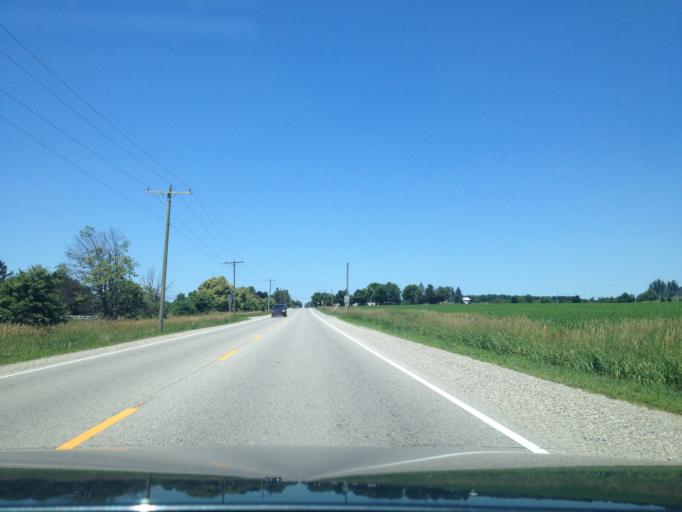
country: CA
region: Ontario
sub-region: Wellington County
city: Guelph
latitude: 43.6644
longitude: -80.2828
